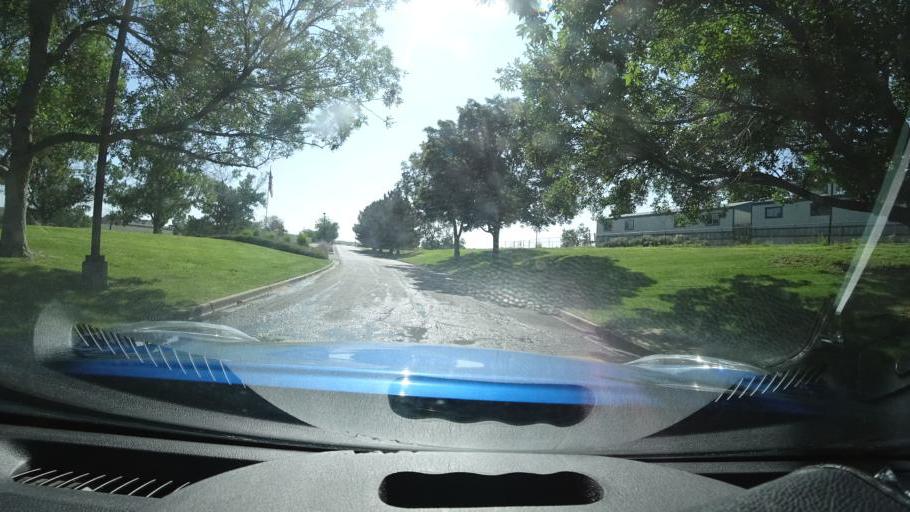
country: US
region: Colorado
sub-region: Adams County
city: Aurora
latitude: 39.7113
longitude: -104.7937
